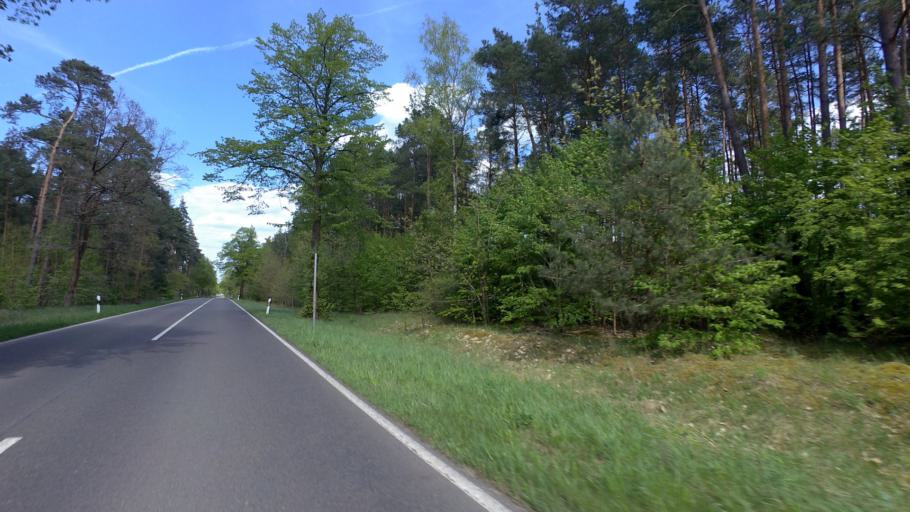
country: DE
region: Brandenburg
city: Milmersdorf
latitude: 53.0825
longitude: 13.6230
